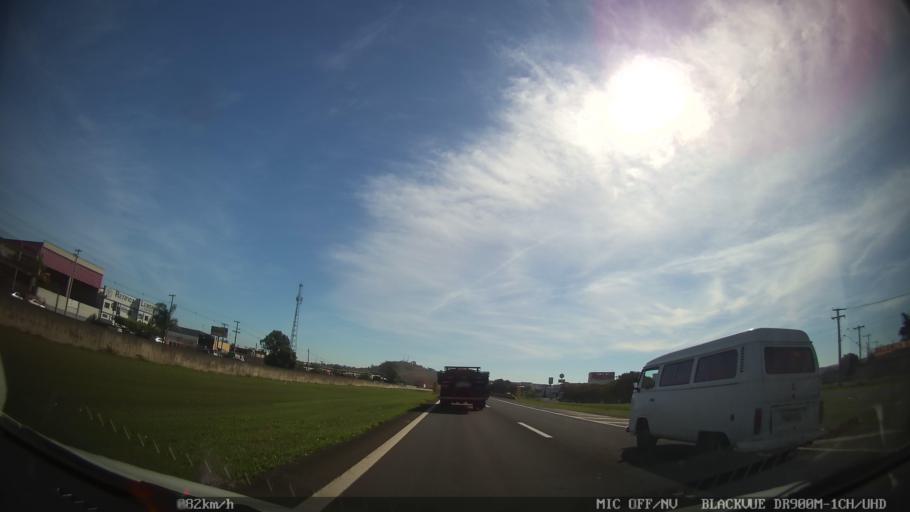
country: BR
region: Sao Paulo
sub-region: Leme
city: Leme
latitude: -22.1770
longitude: -47.3987
